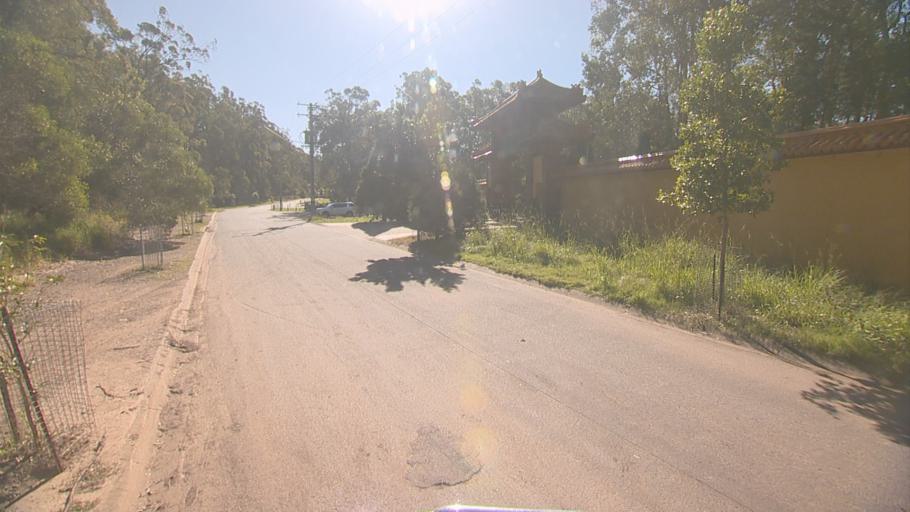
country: AU
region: Queensland
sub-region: Logan
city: Springwood
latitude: -27.6046
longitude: 153.1504
